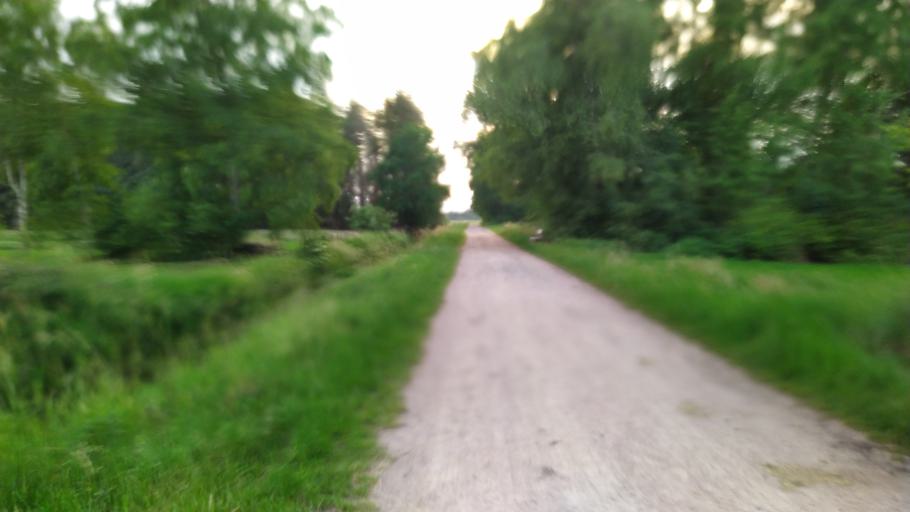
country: DE
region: Lower Saxony
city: Buxtehude
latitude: 53.4816
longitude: 9.6570
